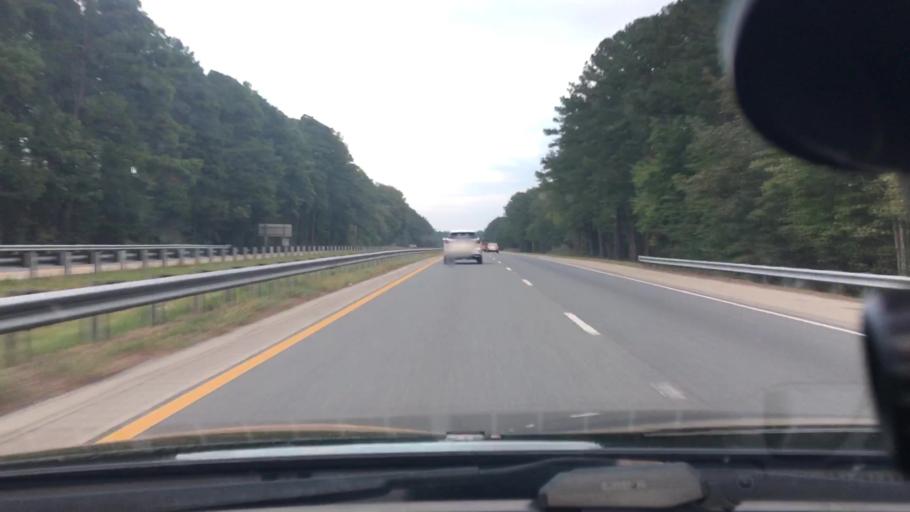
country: US
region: North Carolina
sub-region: Chatham County
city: Pittsboro
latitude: 35.6295
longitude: -79.0710
